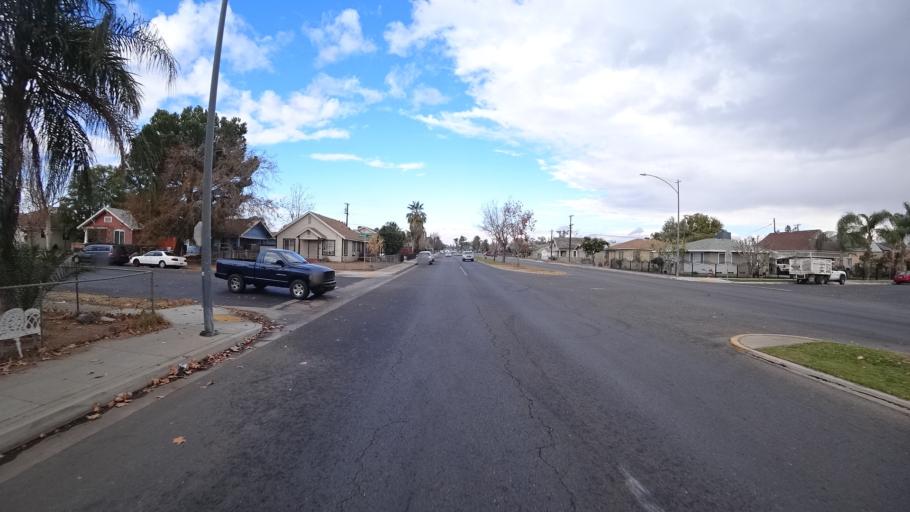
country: US
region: California
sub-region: Kern County
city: Bakersfield
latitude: 35.3823
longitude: -118.9877
